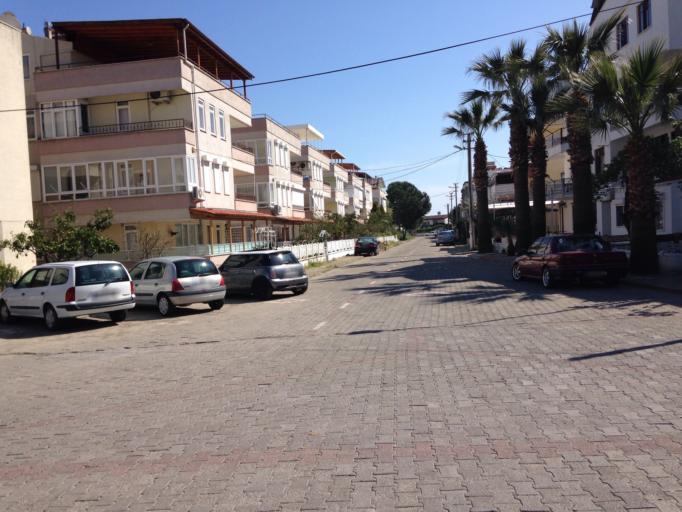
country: TR
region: Balikesir
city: Altinoluk
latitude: 39.5664
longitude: 26.7542
